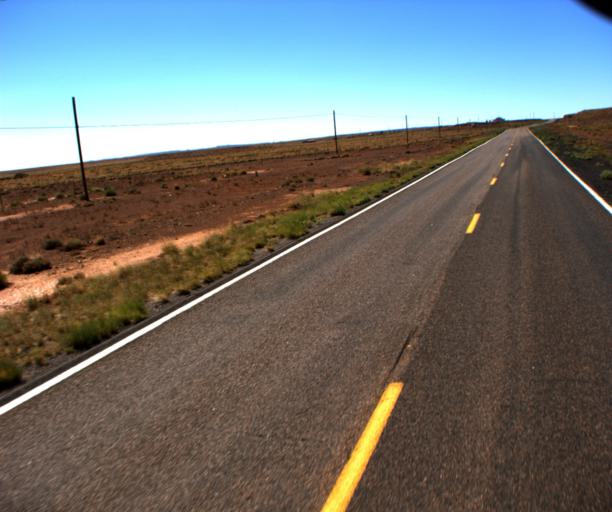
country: US
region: Arizona
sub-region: Coconino County
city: LeChee
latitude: 35.1461
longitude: -110.8944
